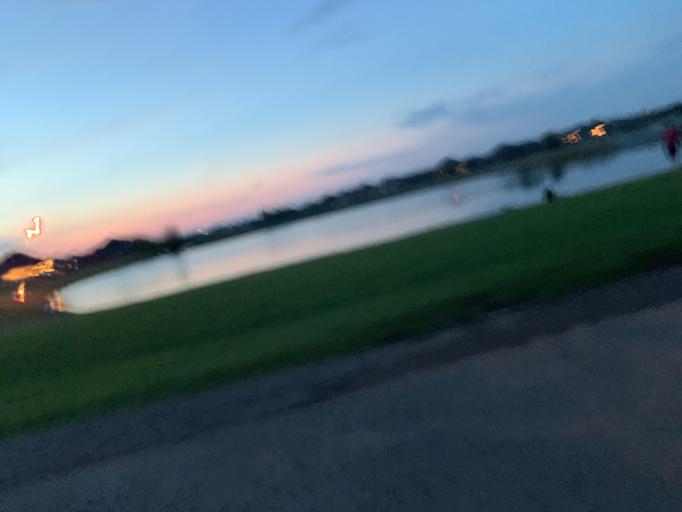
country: US
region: Oklahoma
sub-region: Oklahoma County
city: Edmond
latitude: 35.6620
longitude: -97.5725
